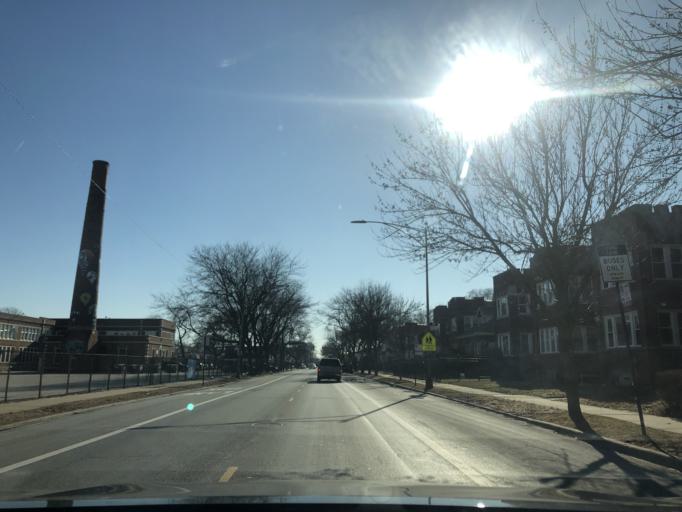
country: US
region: Indiana
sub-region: Lake County
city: Whiting
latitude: 41.7497
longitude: -87.5760
